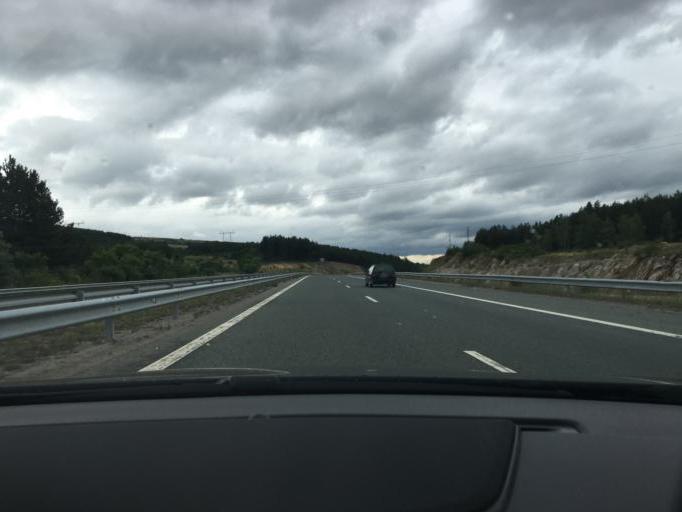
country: BG
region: Pernik
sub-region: Obshtina Pernik
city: Pernik
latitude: 42.5021
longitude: 23.1399
